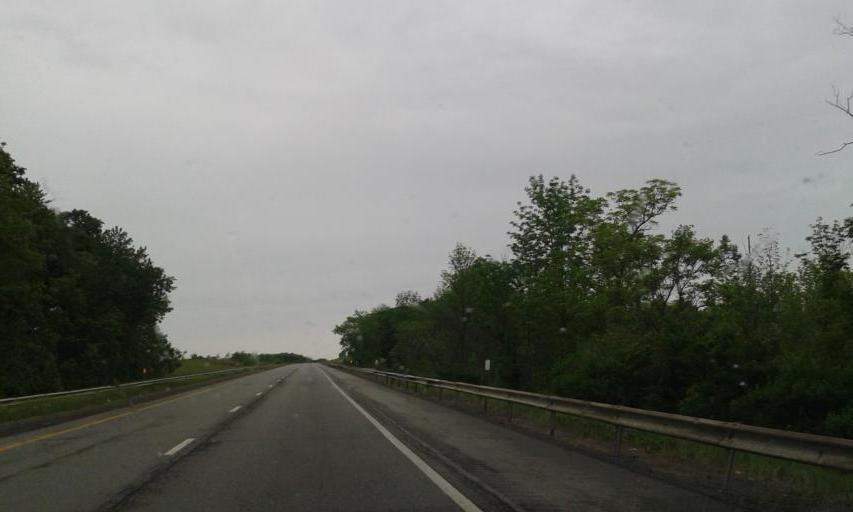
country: US
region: New York
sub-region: Genesee County
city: Bergen
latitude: 43.0295
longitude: -77.9275
